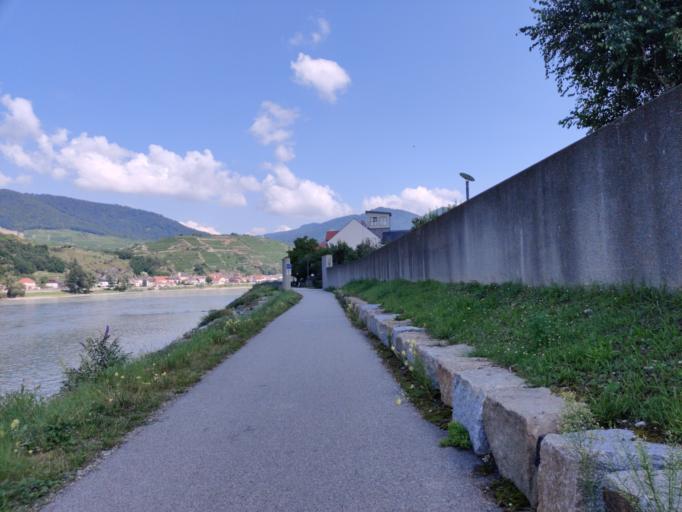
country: AT
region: Lower Austria
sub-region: Politischer Bezirk Krems
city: Spitz
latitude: 48.3521
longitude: 15.4109
